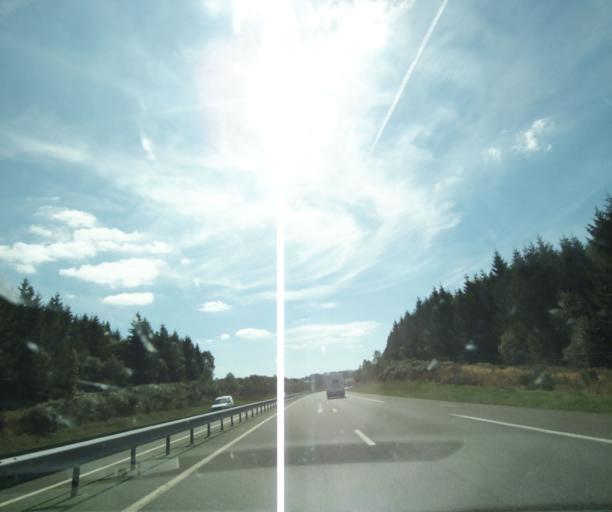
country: FR
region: Auvergne
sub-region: Departement du Puy-de-Dome
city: Saint-Sauves-d'Auvergne
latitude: 45.6846
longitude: 2.6960
